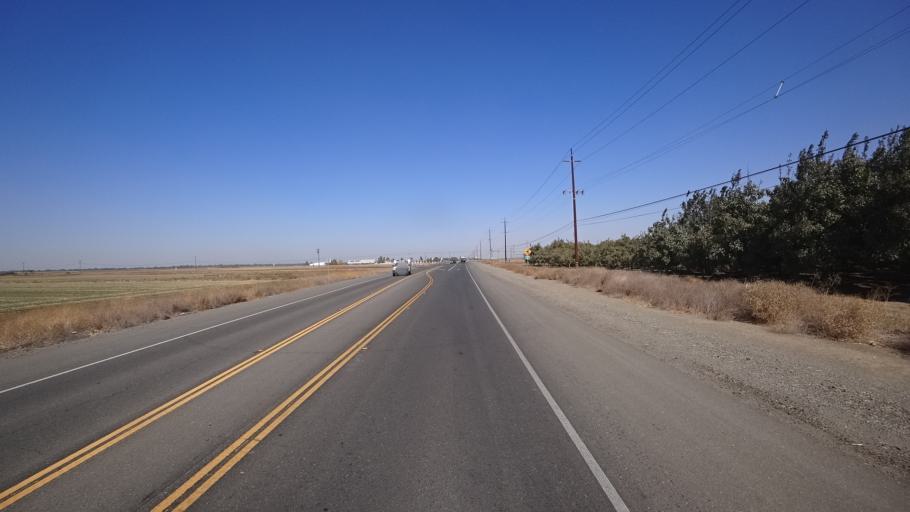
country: US
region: California
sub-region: Yolo County
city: Davis
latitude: 38.5878
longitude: -121.7303
